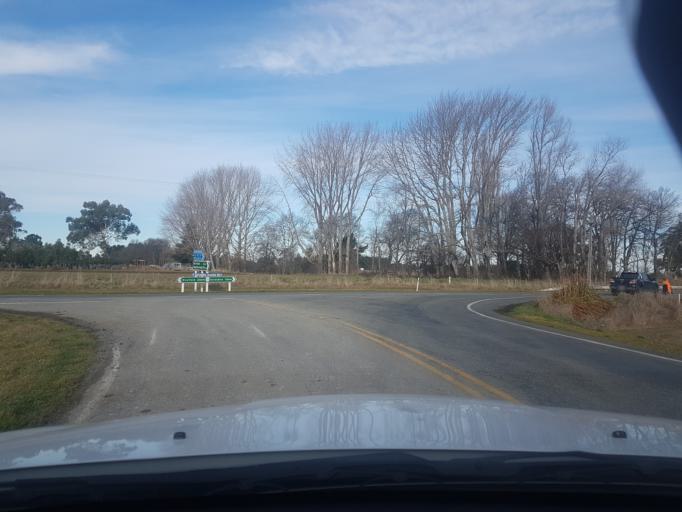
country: NZ
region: Canterbury
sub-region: Timaru District
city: Pleasant Point
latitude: -44.0147
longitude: 171.2781
